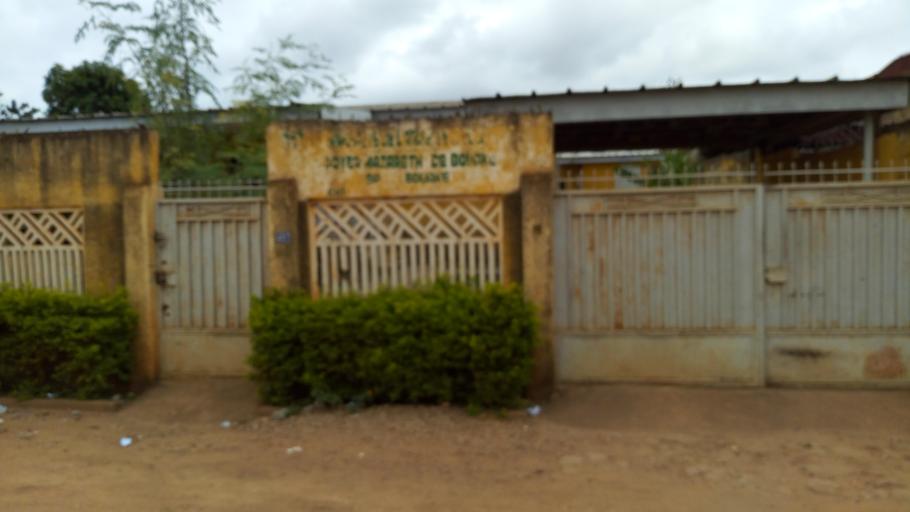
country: CI
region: Vallee du Bandama
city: Bouake
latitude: 7.6824
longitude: -5.0537
